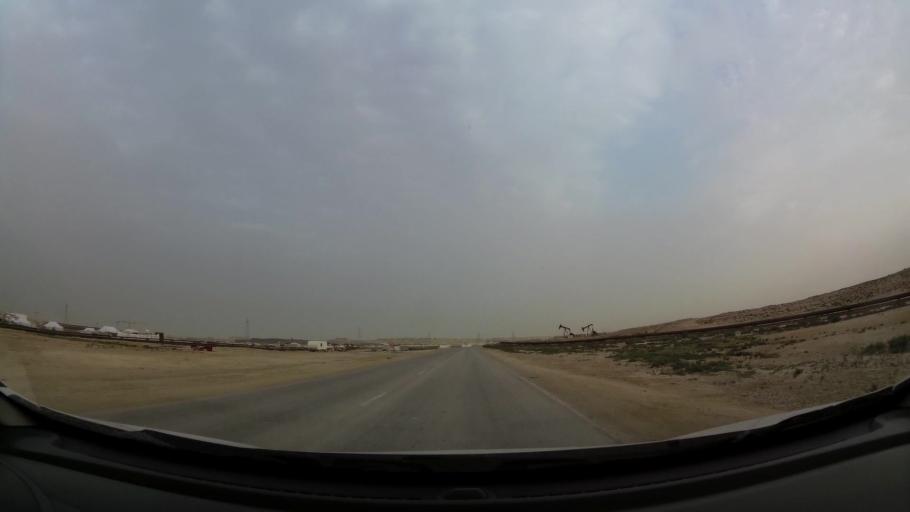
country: BH
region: Central Governorate
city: Dar Kulayb
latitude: 26.0151
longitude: 50.5773
